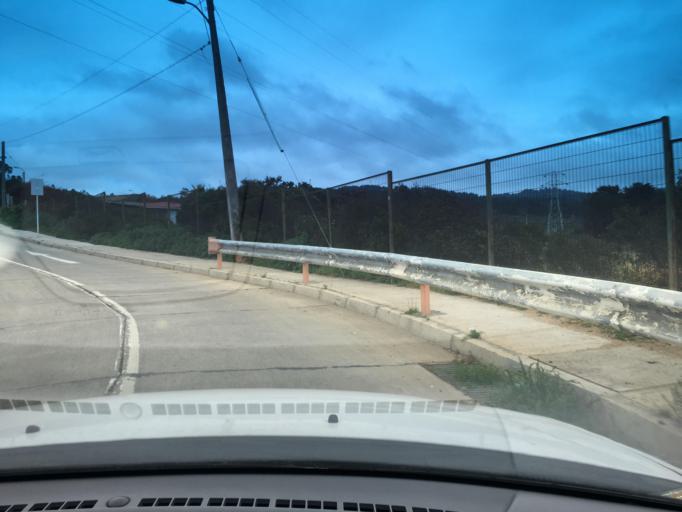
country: CL
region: Valparaiso
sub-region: Provincia de Valparaiso
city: Valparaiso
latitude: -33.1032
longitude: -71.6734
